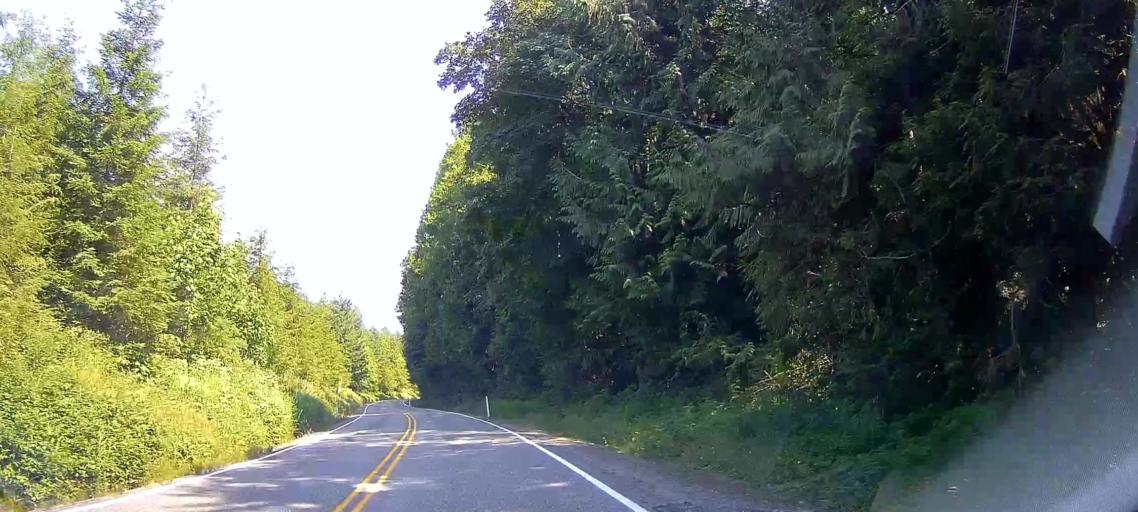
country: US
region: Washington
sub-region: Snohomish County
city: Arlington Heights
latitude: 48.3376
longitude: -122.0464
